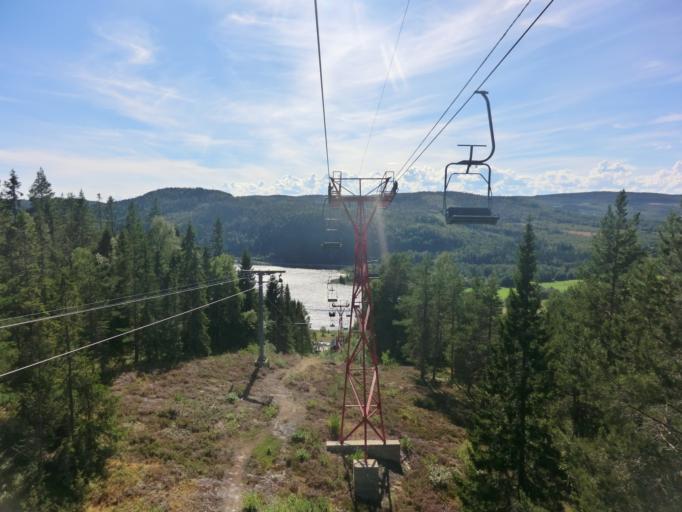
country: SE
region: Vaesternorrland
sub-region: Kramfors Kommun
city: Nordingra
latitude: 63.0730
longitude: 18.3383
